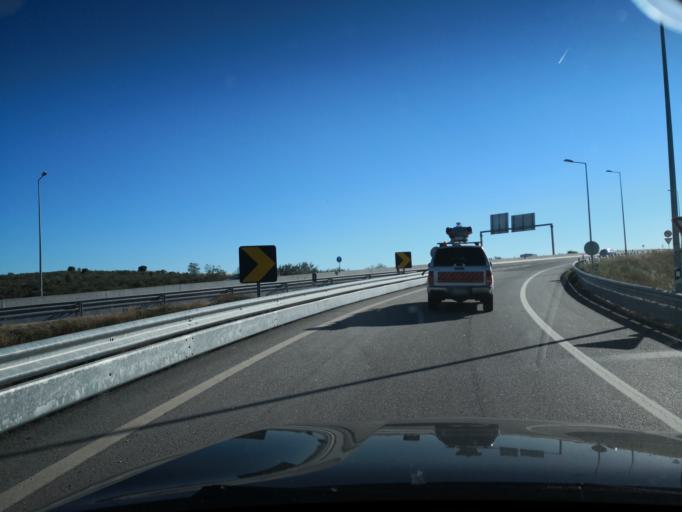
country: PT
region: Braganca
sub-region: Mirandela
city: Mirandela
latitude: 41.4763
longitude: -7.2233
